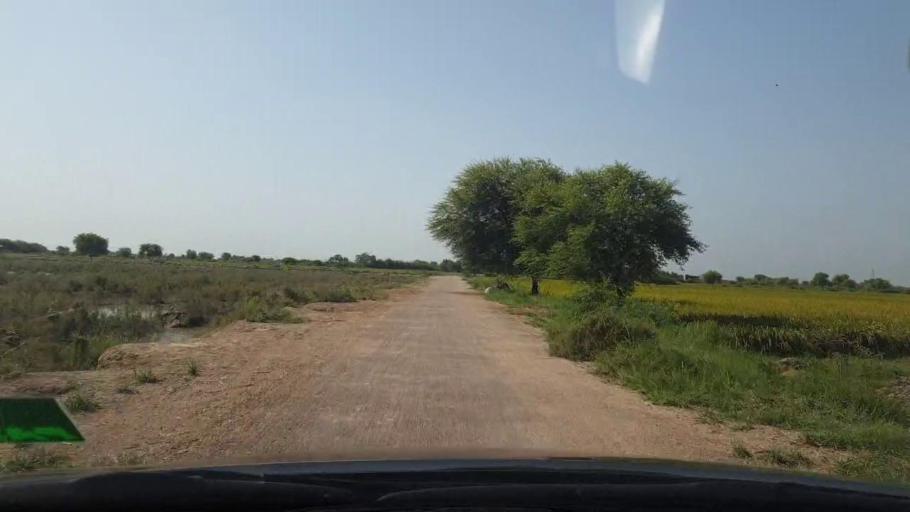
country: PK
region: Sindh
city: Tando Bago
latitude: 24.7419
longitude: 68.9725
